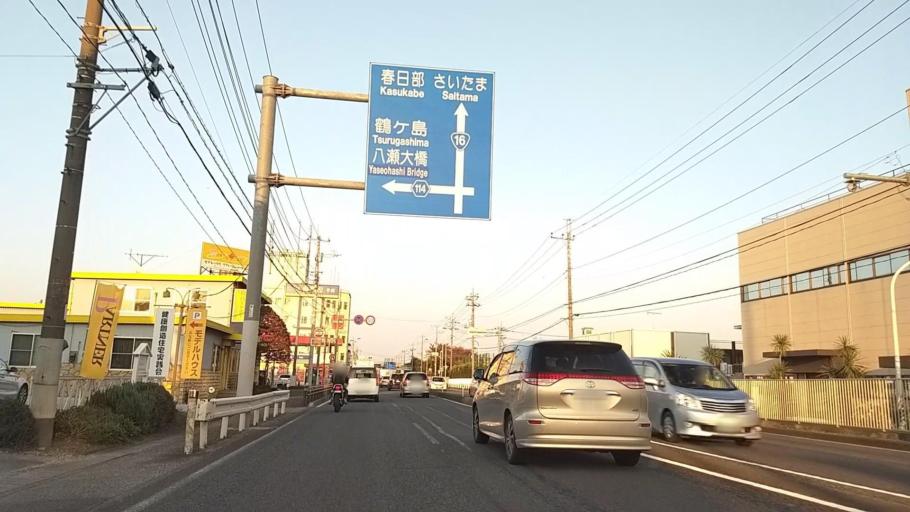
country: JP
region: Saitama
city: Kawagoe
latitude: 35.8882
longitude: 139.4455
